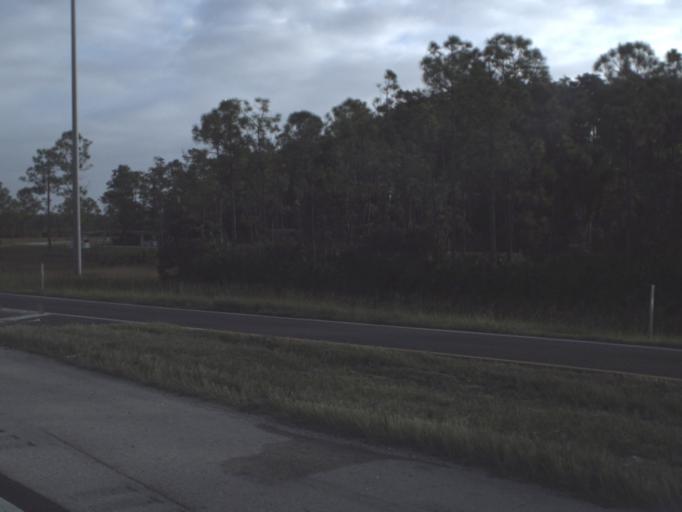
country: US
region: Florida
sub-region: Lee County
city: Gateway
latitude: 26.5510
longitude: -81.7949
